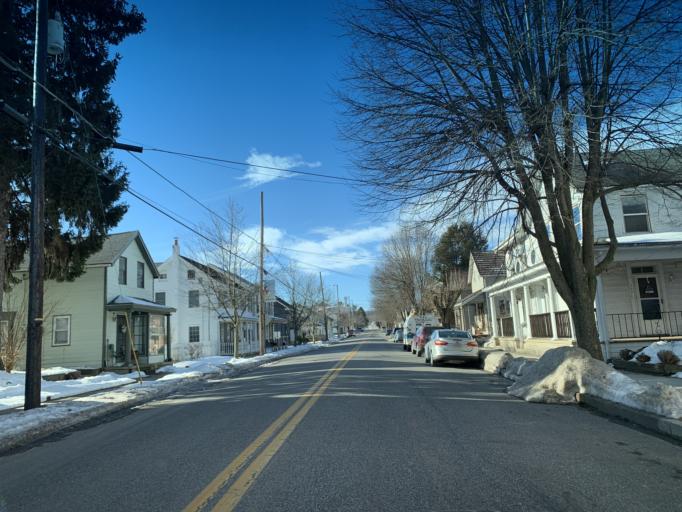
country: US
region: Pennsylvania
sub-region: York County
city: Dover
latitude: 40.0511
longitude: -76.9429
